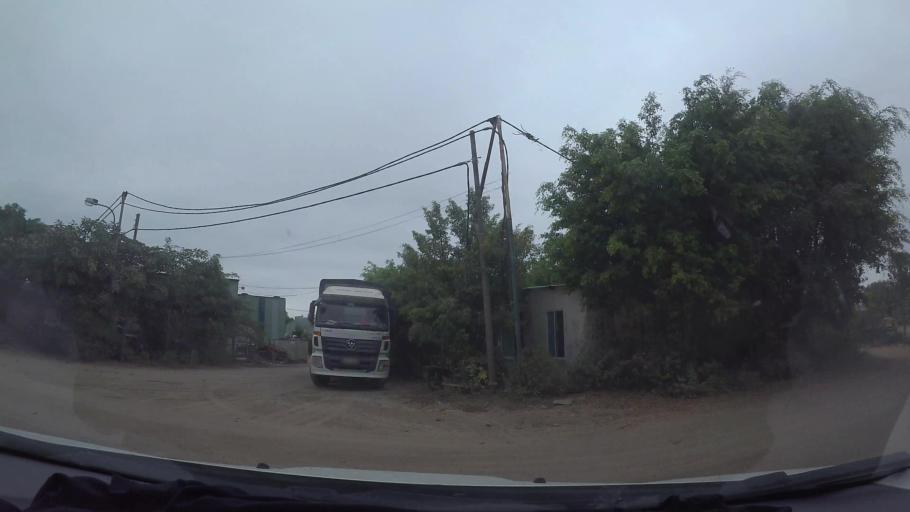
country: VN
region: Da Nang
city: Lien Chieu
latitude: 16.0694
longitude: 108.1393
